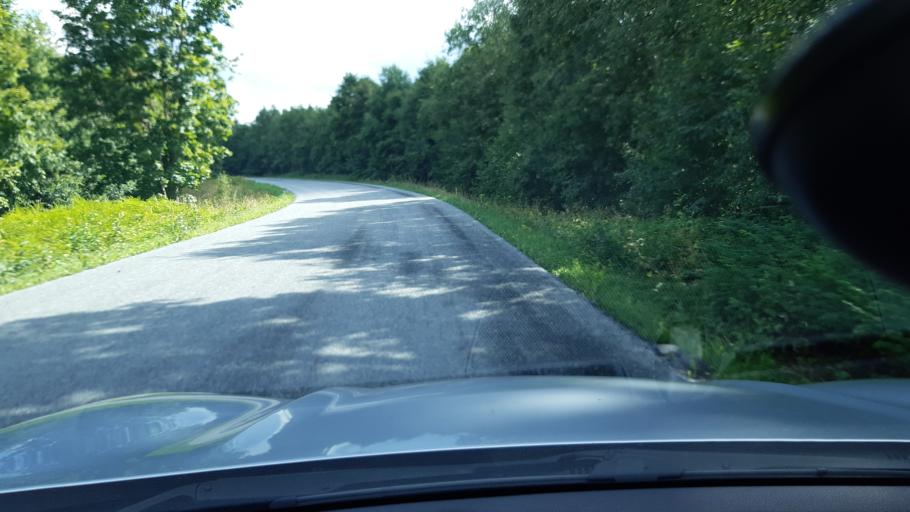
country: EE
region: Raplamaa
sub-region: Kehtna vald
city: Kehtna
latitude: 58.9041
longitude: 25.0580
